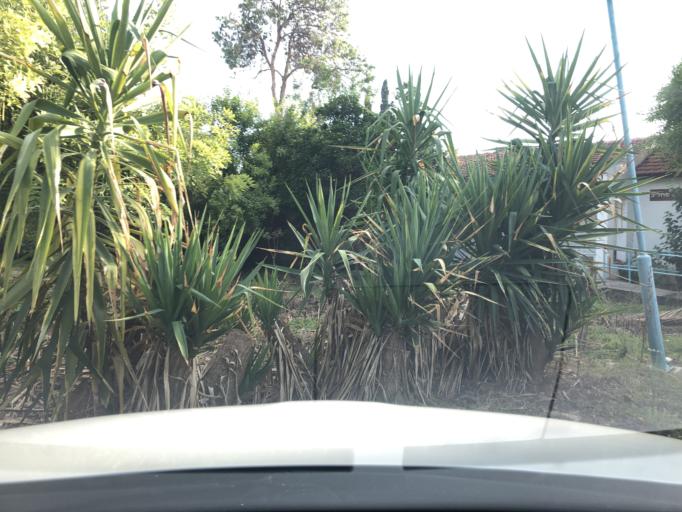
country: IL
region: Northern District
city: Yavne'el
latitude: 32.6604
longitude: 35.5821
